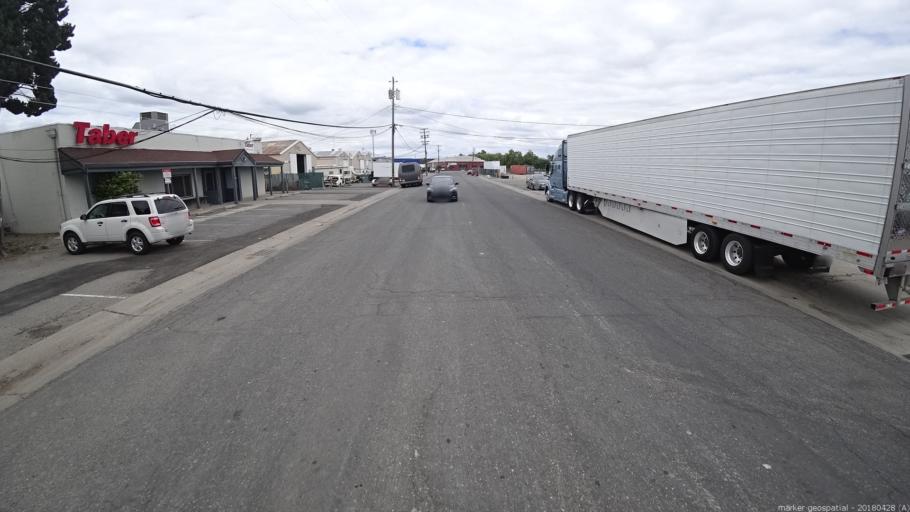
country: US
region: California
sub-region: Yolo County
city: West Sacramento
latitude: 38.5826
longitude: -121.5527
